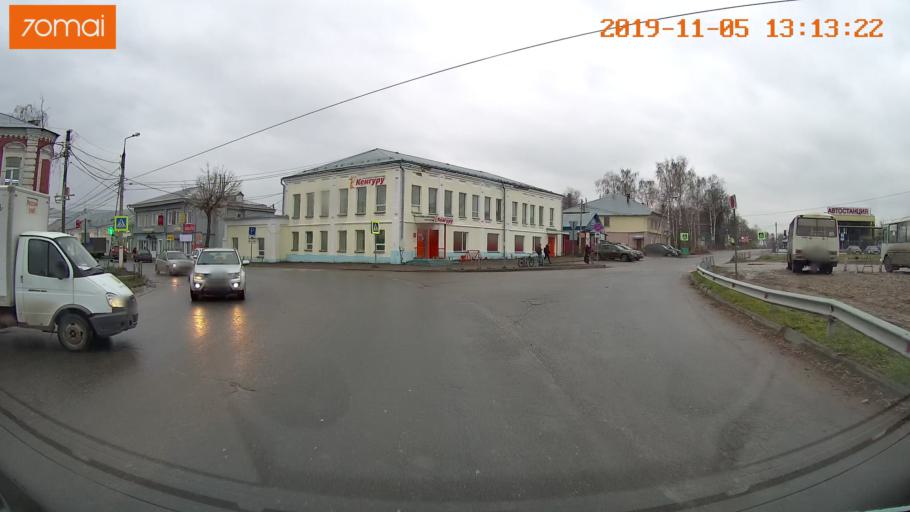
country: RU
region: Ivanovo
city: Shuya
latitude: 56.8515
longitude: 41.3539
